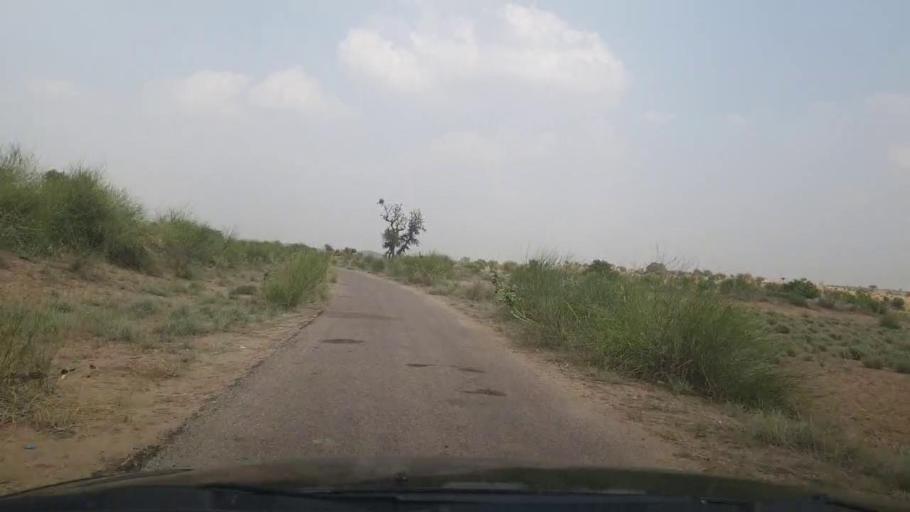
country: PK
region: Sindh
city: Islamkot
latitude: 24.9321
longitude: 70.5709
